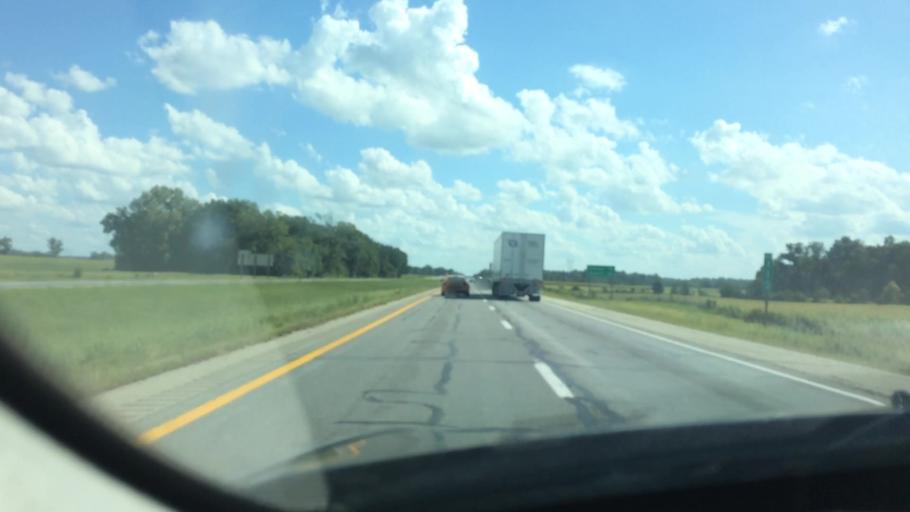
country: US
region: Ohio
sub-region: Auglaize County
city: Wapakoneta
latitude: 40.5429
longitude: -84.1698
